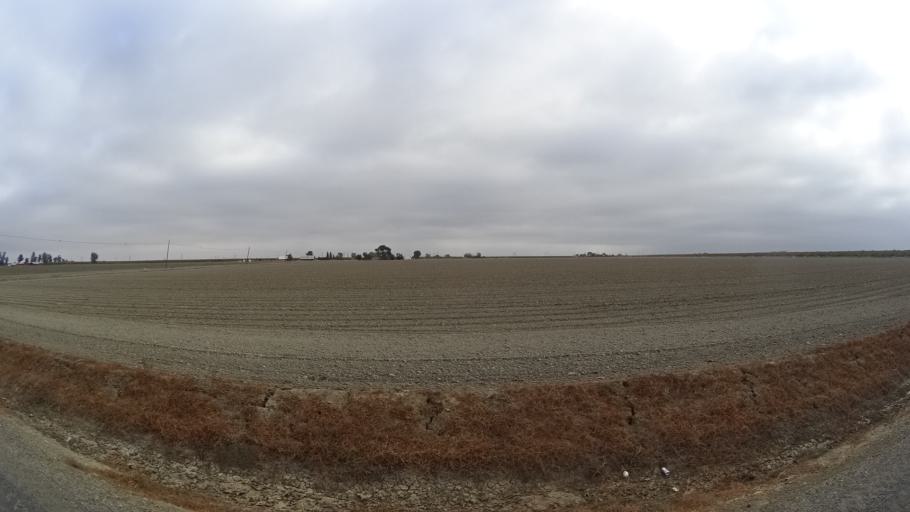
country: US
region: California
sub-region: Yolo County
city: Esparto
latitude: 38.7358
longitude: -122.0059
